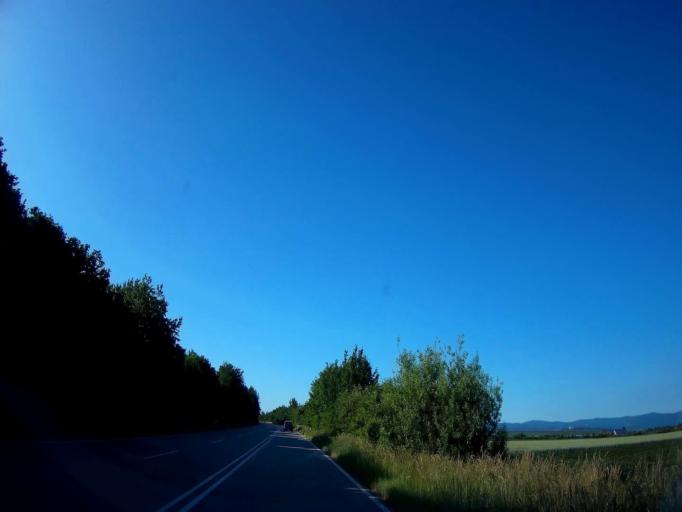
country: DE
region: Bavaria
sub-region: Lower Bavaria
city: Alterhofen
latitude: 48.8546
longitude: 12.6315
